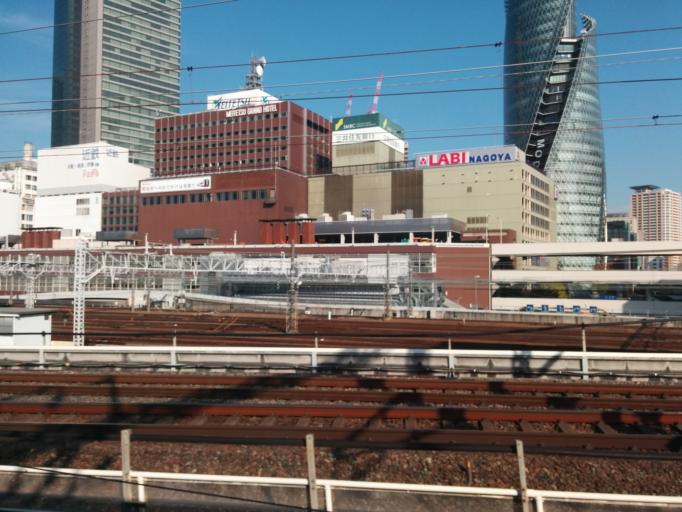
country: JP
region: Aichi
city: Nagoya-shi
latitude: 35.1673
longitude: 136.8831
